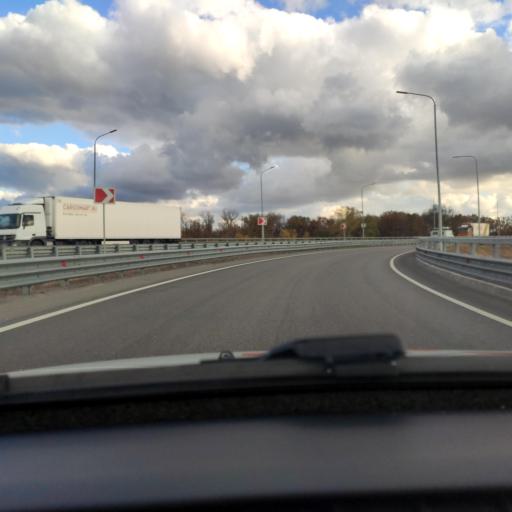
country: RU
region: Voronezj
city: Podgornoye
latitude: 51.8409
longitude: 39.2177
